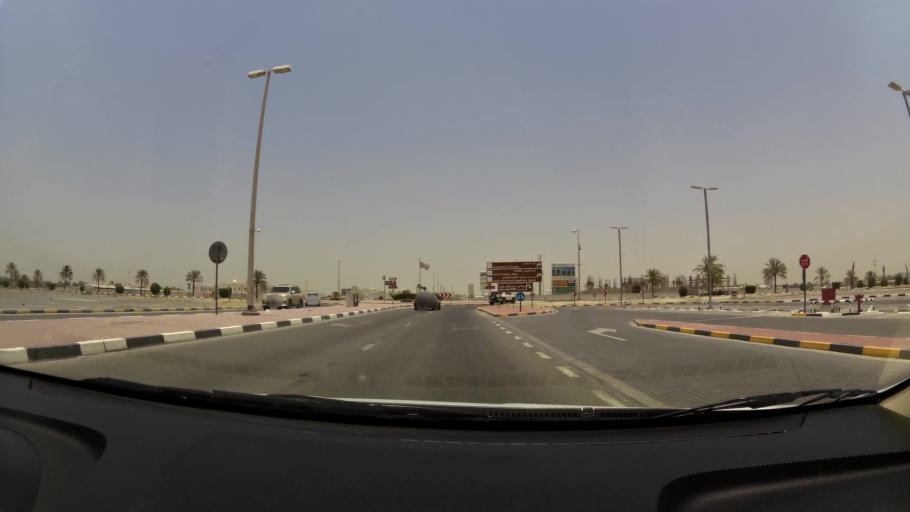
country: AE
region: Ajman
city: Ajman
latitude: 25.4047
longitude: 55.4831
